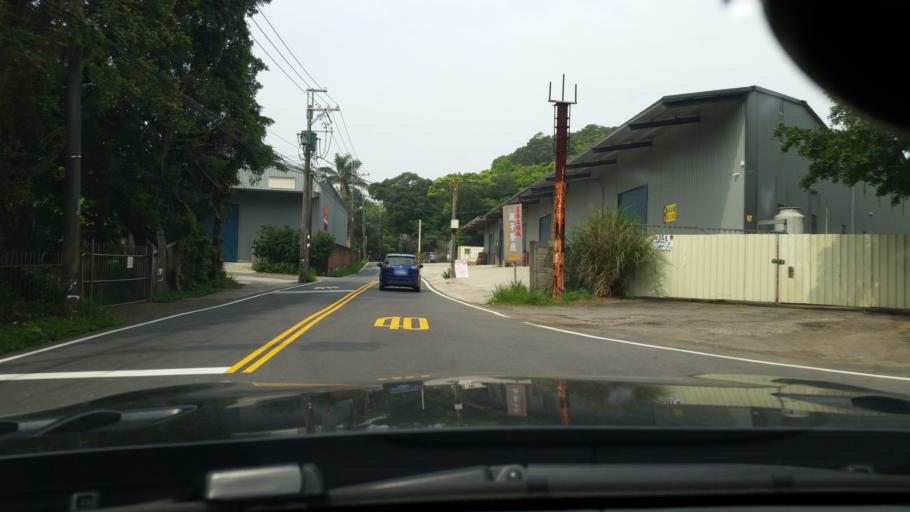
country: TW
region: Taiwan
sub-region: Taoyuan
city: Taoyuan
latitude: 25.0599
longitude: 121.3289
